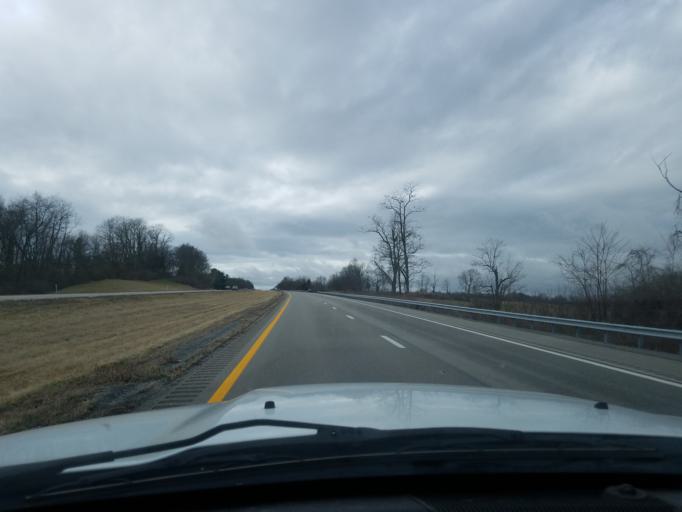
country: US
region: Kentucky
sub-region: Montgomery County
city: Mount Sterling
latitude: 38.0717
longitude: -83.9998
